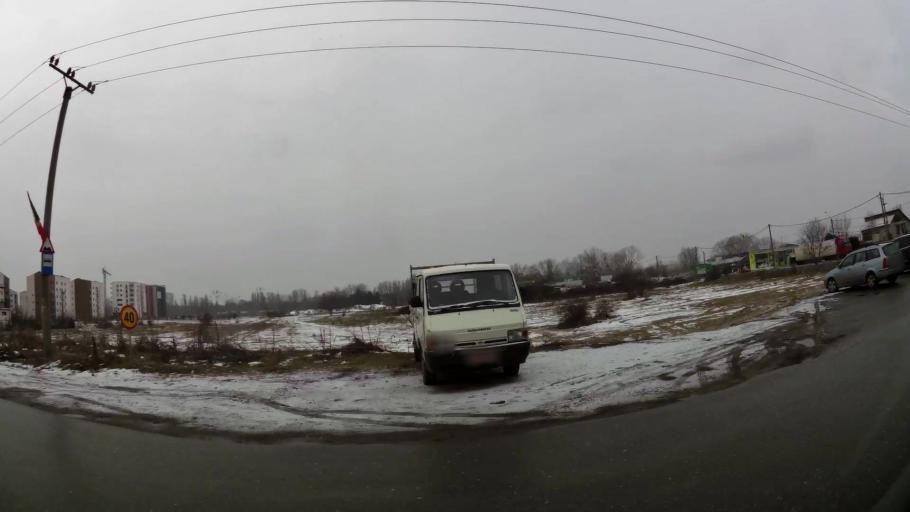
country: RO
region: Dambovita
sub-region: Municipiul Targoviste
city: Targoviste
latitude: 44.9421
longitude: 25.4610
